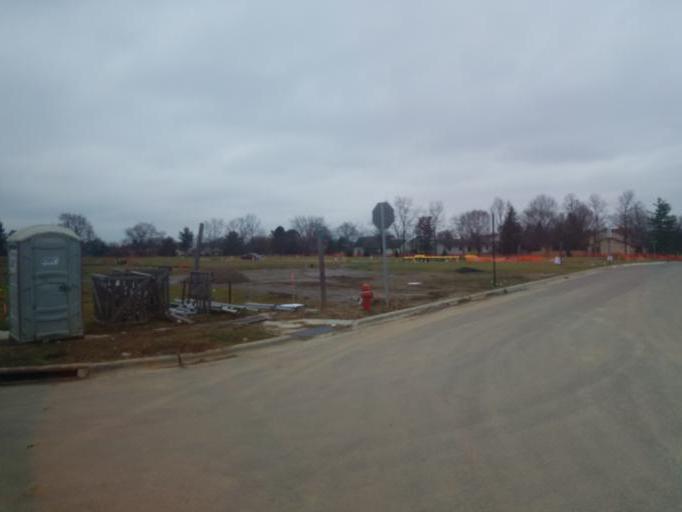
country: US
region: Ohio
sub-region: Franklin County
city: Westerville
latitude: 40.1314
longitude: -82.9641
